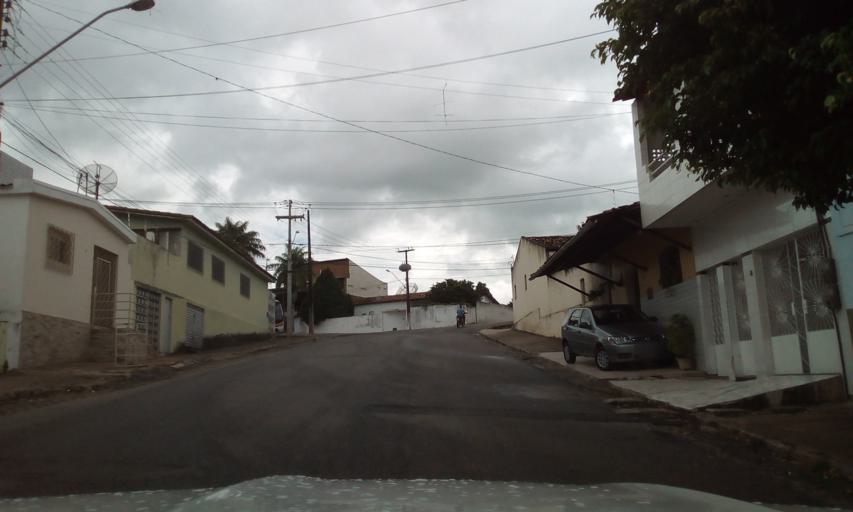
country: BR
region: Paraiba
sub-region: Guarabira
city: Guarabira
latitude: -6.8474
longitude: -35.4878
